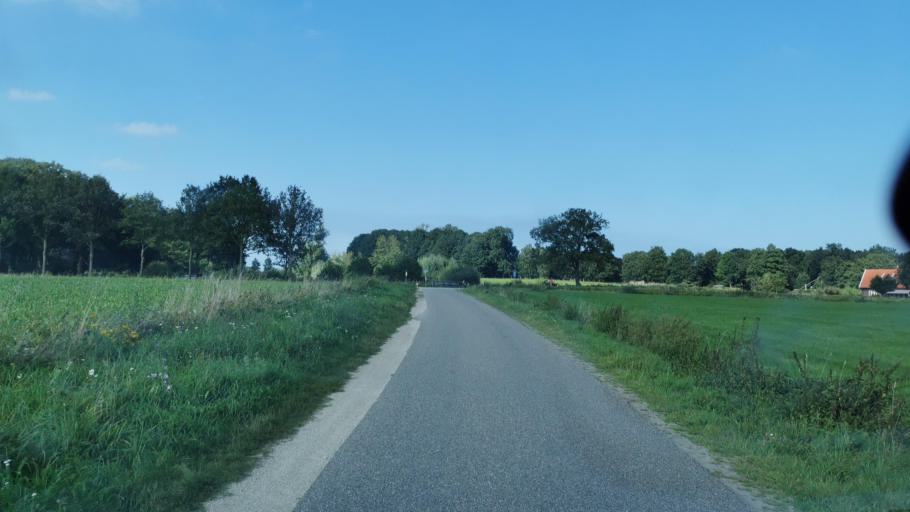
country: DE
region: Lower Saxony
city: Getelo
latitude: 52.4026
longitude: 6.8793
